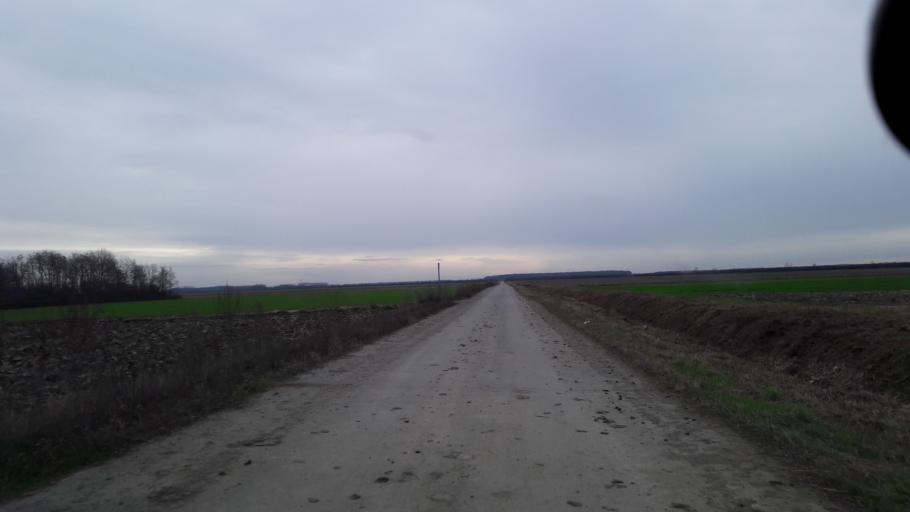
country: HR
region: Osjecko-Baranjska
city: Vladislavci
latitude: 45.4423
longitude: 18.5653
